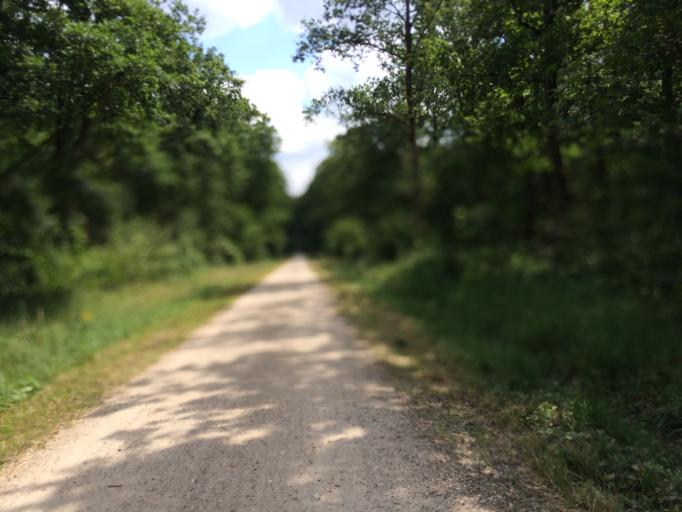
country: FR
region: Ile-de-France
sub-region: Departement de l'Essonne
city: Tigery
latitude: 48.6614
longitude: 2.5082
